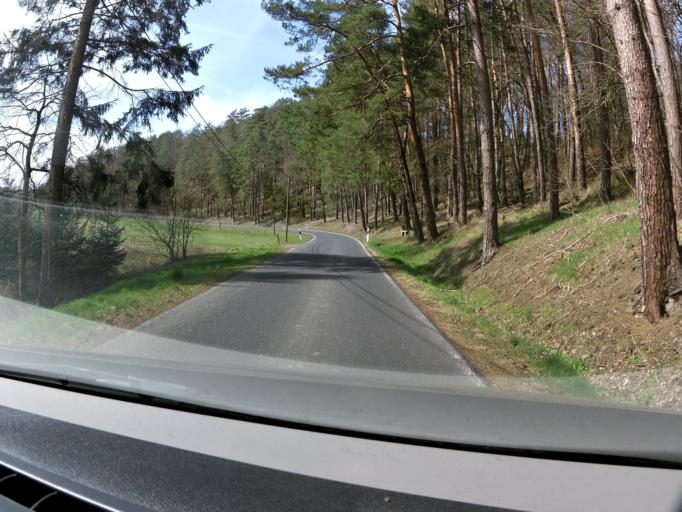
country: DE
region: Thuringia
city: Frauensee
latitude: 50.8663
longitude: 10.1355
